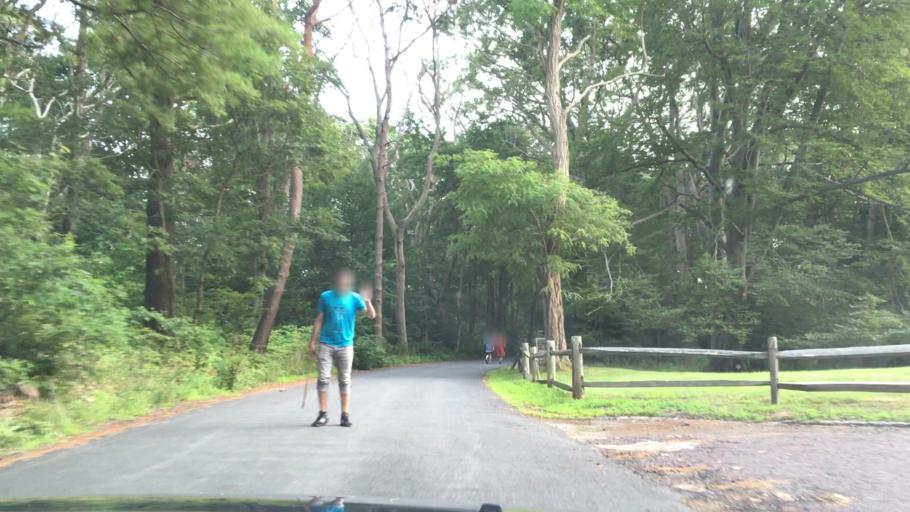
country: US
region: Massachusetts
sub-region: Essex County
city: Gloucester
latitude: 42.5746
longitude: -70.7260
